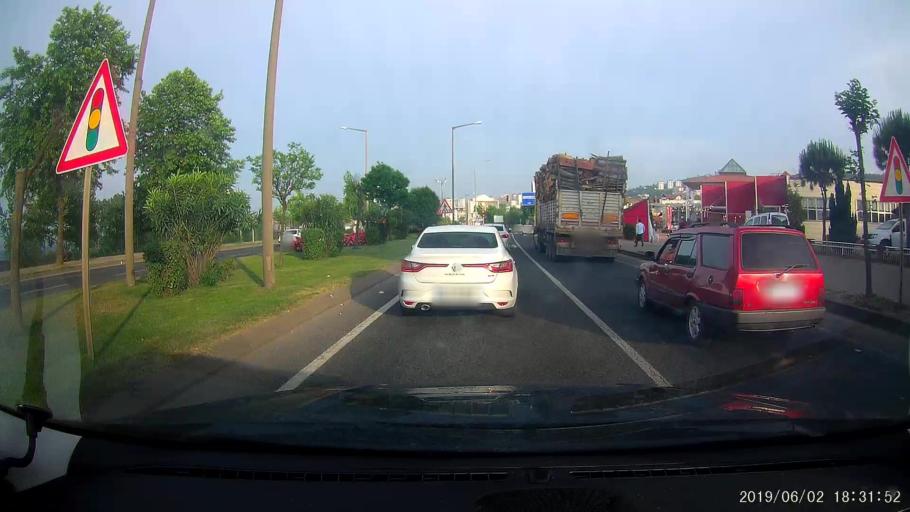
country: TR
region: Ordu
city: Fatsa
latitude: 41.0364
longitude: 37.4934
